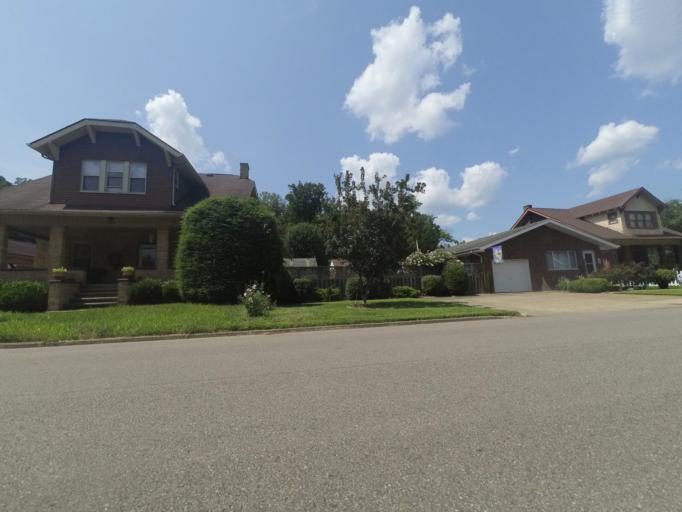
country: US
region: West Virginia
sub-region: Cabell County
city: Huntington
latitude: 38.3988
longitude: -82.4267
